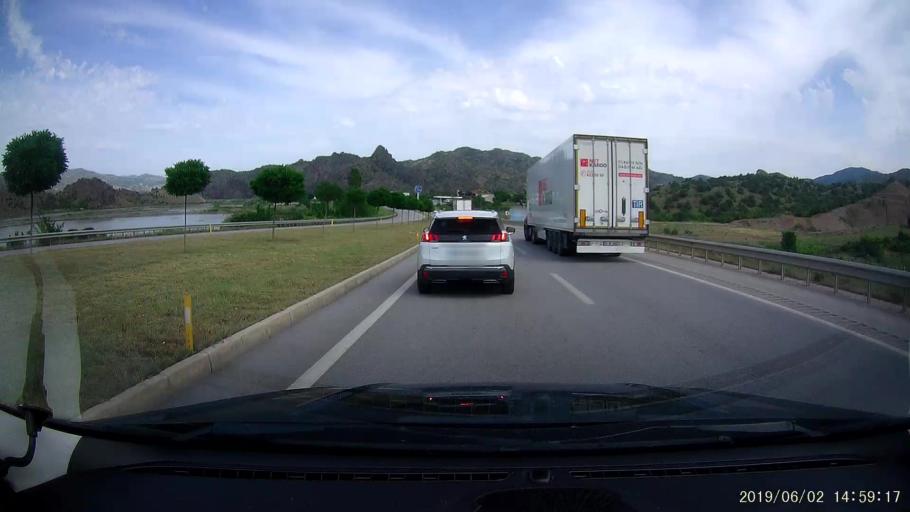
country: TR
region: Corum
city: Osmancik
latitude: 40.9715
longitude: 34.6937
